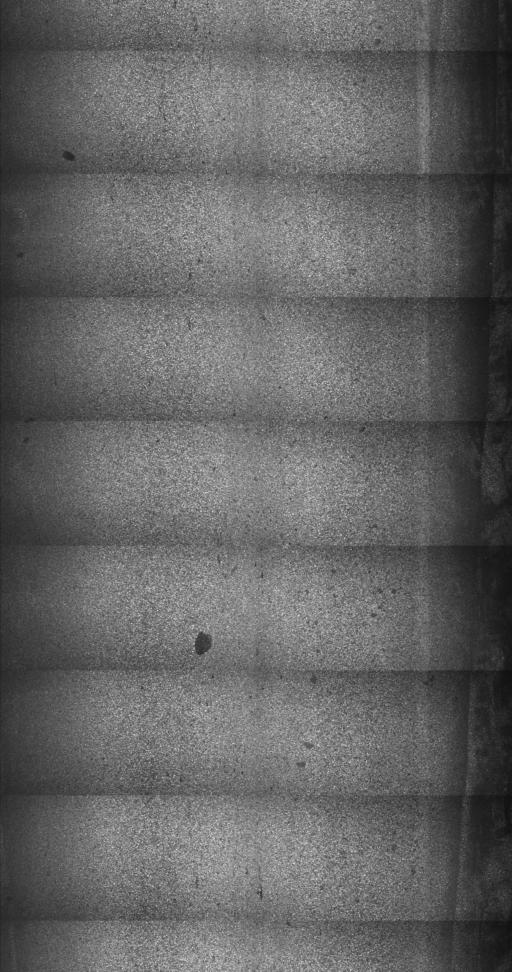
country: US
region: Vermont
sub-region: Rutland County
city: Rutland
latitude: 43.6796
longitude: -72.8108
